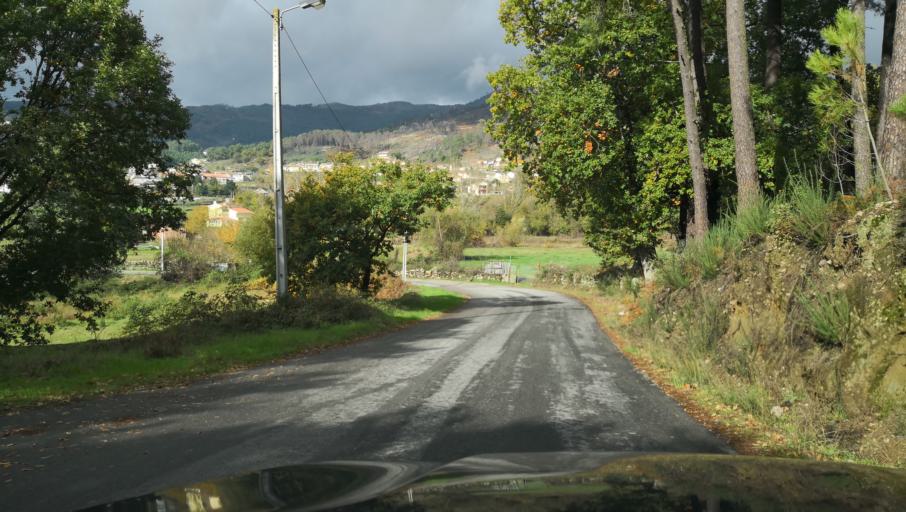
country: PT
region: Vila Real
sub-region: Vila Real
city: Vila Real
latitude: 41.3172
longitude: -7.7552
